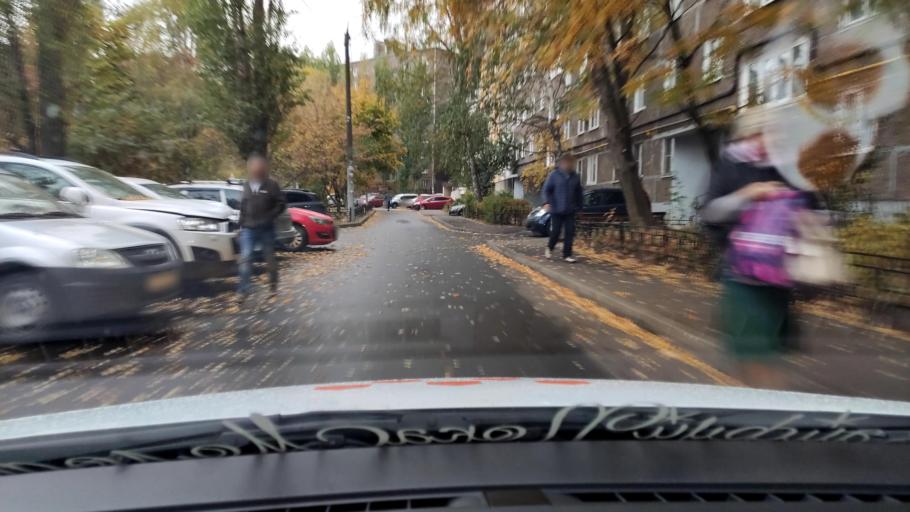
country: RU
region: Voronezj
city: Podgornoye
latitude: 51.7029
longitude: 39.1433
